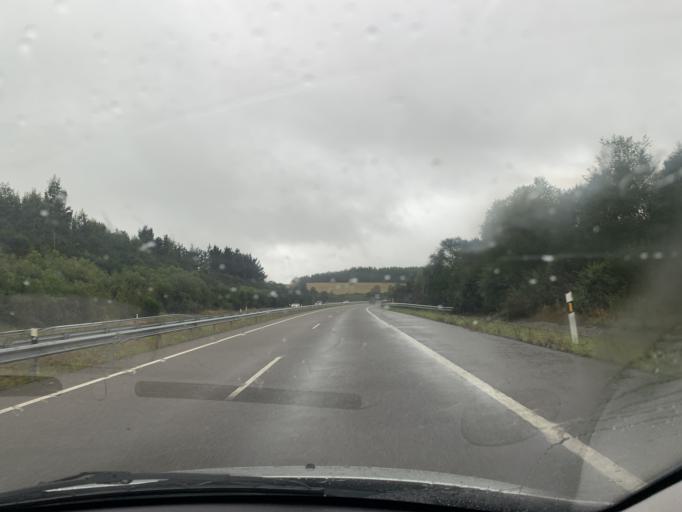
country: ES
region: Galicia
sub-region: Provincia de Lugo
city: Abadin
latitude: 43.3600
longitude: -7.4593
